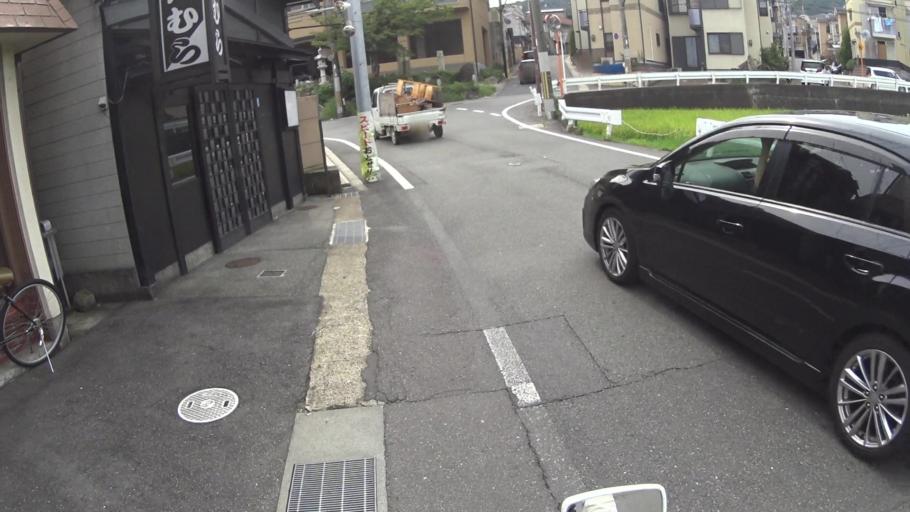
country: JP
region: Kyoto
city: Kyoto
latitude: 34.9798
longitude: 135.7975
